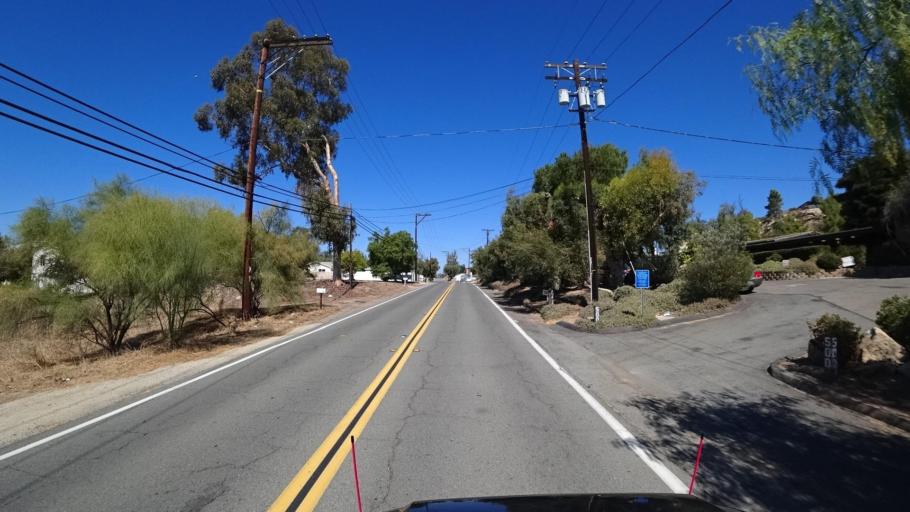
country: US
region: California
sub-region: San Diego County
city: Ramona
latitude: 33.0462
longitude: -116.8560
